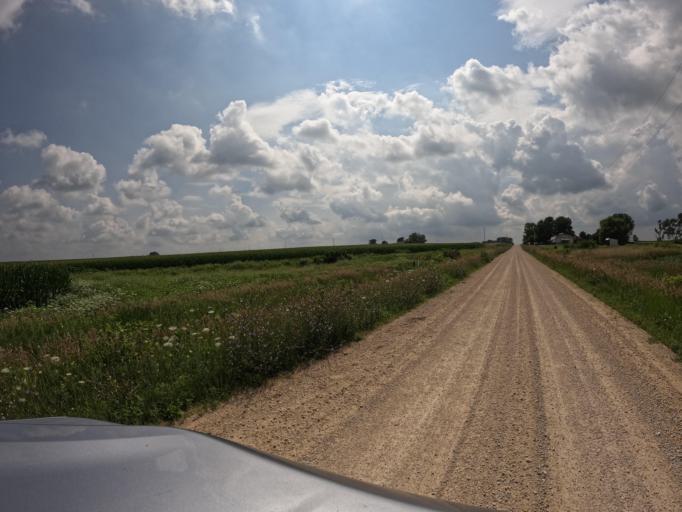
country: US
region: Iowa
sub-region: Clinton County
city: Camanche
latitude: 41.7720
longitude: -90.3509
